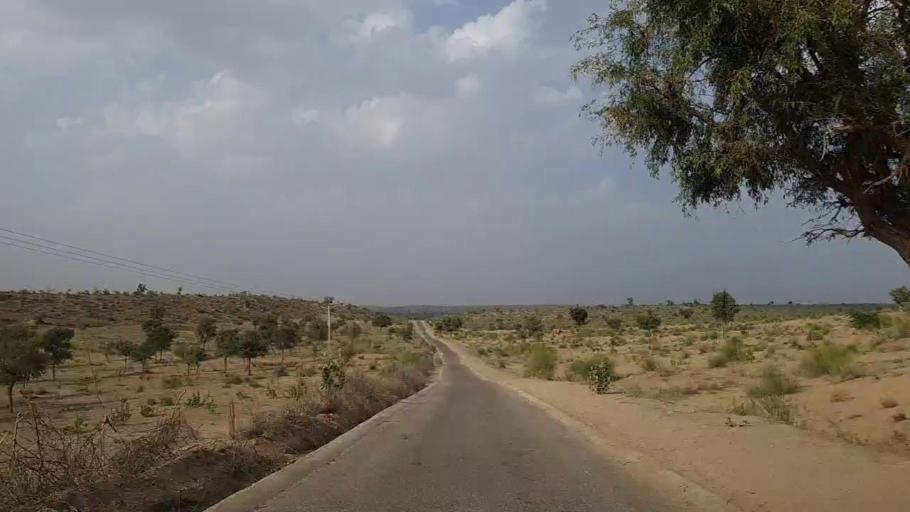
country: PK
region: Sindh
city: Islamkot
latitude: 24.7855
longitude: 70.2000
